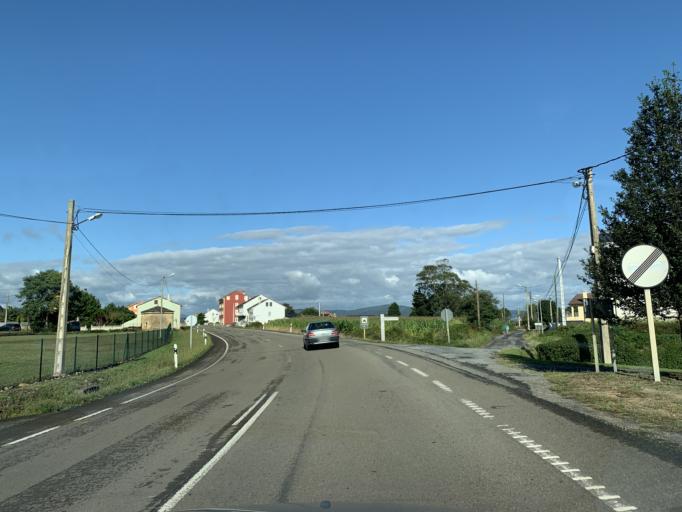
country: ES
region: Galicia
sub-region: Provincia de Lugo
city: Barreiros
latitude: 43.5455
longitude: -7.1970
